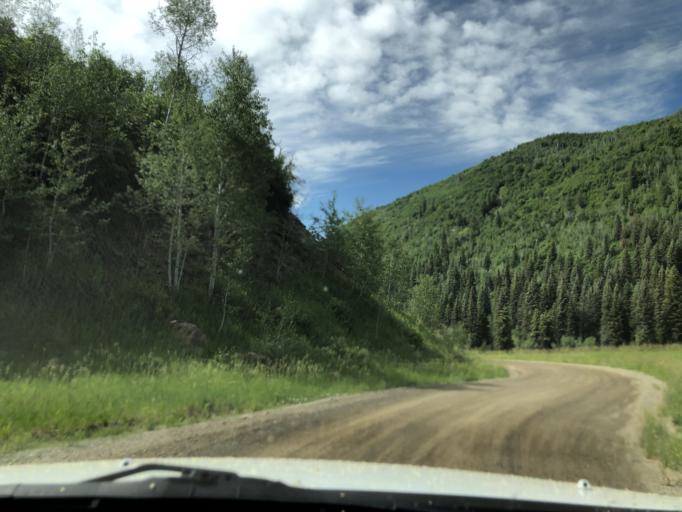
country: US
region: Colorado
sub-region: Delta County
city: Paonia
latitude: 38.9936
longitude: -107.3507
